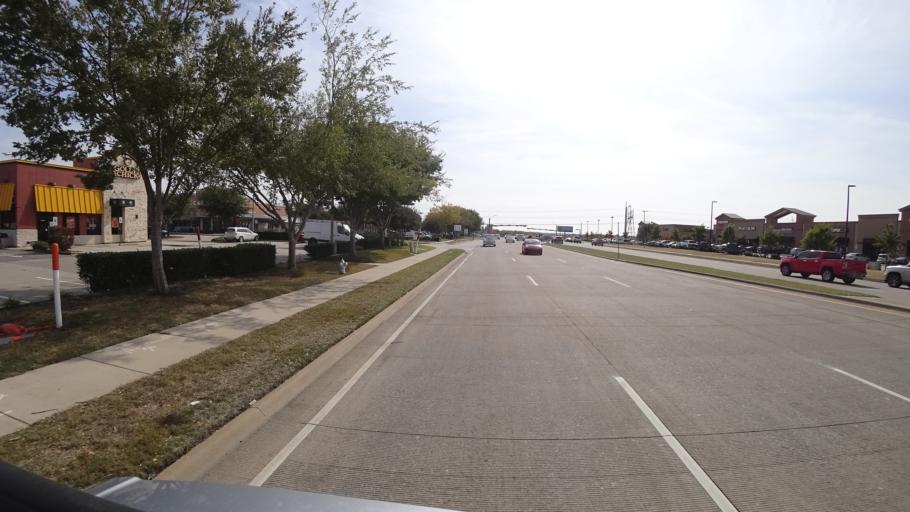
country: US
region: Texas
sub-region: Denton County
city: The Colony
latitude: 33.0636
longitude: -96.8874
